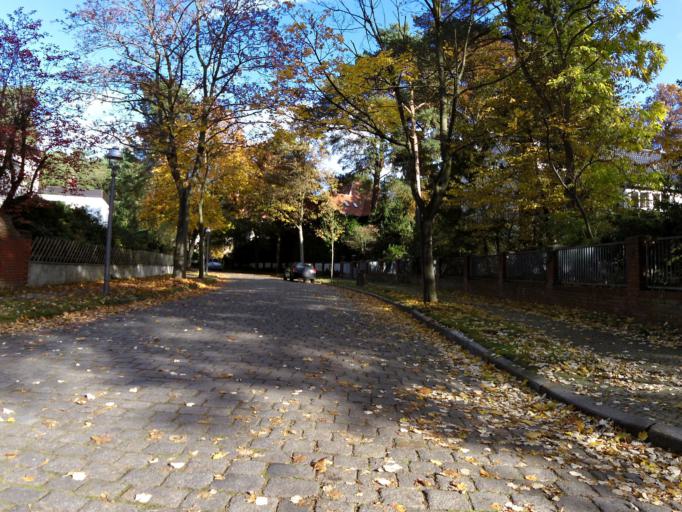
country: DE
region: Berlin
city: Zehlendorf Bezirk
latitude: 52.4428
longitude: 13.2326
